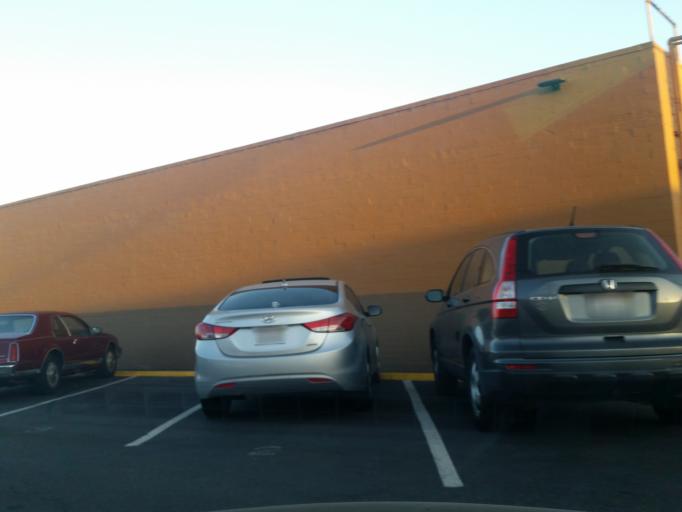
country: US
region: California
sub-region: San Diego County
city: San Diego
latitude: 32.7479
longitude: -117.1288
